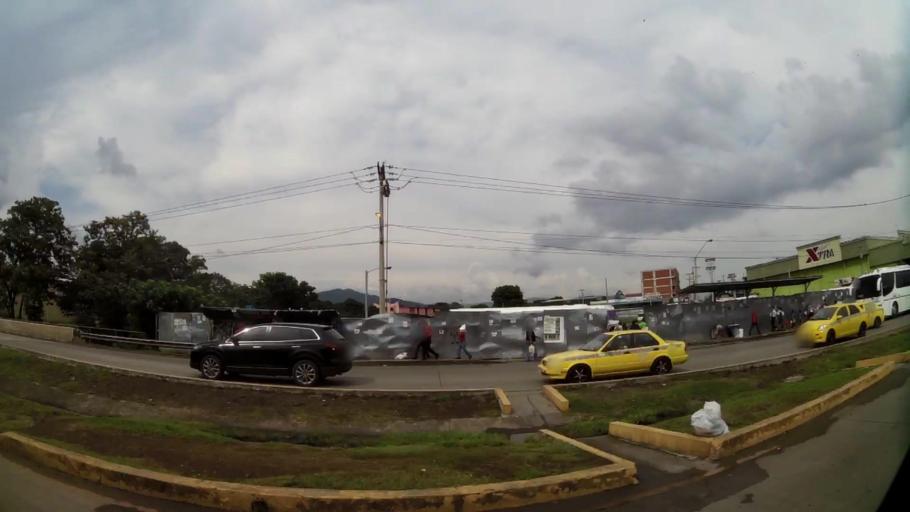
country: PA
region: Panama
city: Tocumen
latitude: 9.1032
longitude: -79.3681
